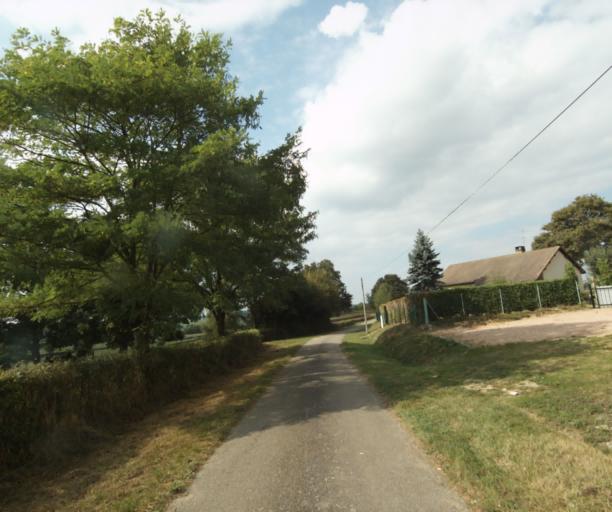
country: FR
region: Bourgogne
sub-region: Departement de Saone-et-Loire
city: Palinges
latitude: 46.4992
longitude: 4.1931
